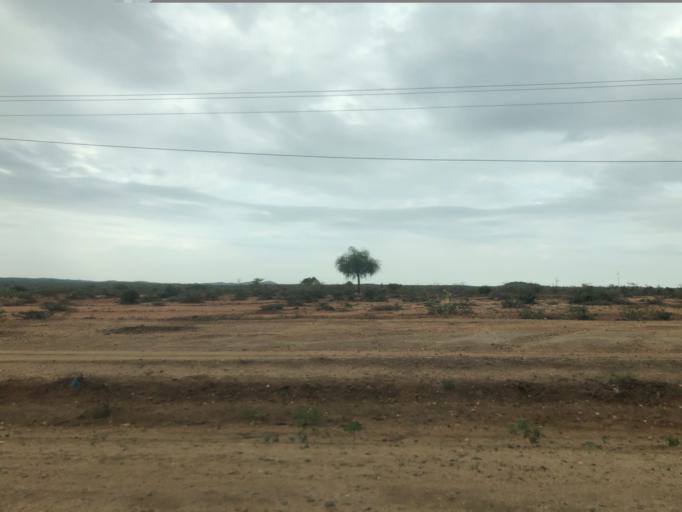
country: ET
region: Southern Nations, Nationalities, and People's Region
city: Turmi
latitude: 4.9731
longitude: 36.4855
